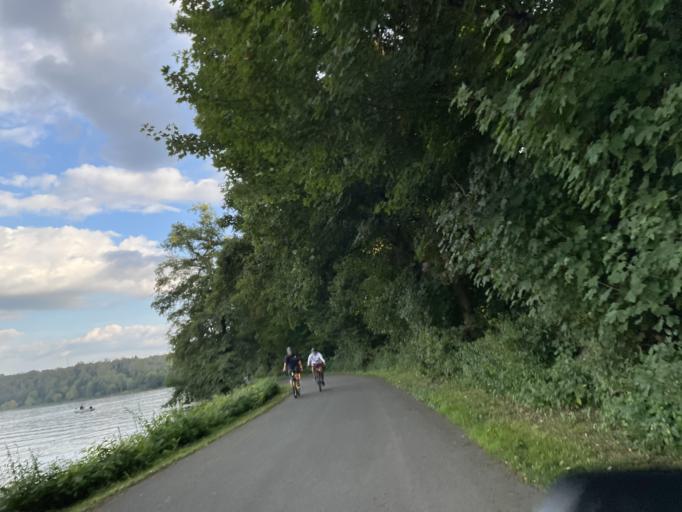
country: DE
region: North Rhine-Westphalia
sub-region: Regierungsbezirk Dusseldorf
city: Velbert
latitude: 51.3912
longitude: 7.0586
